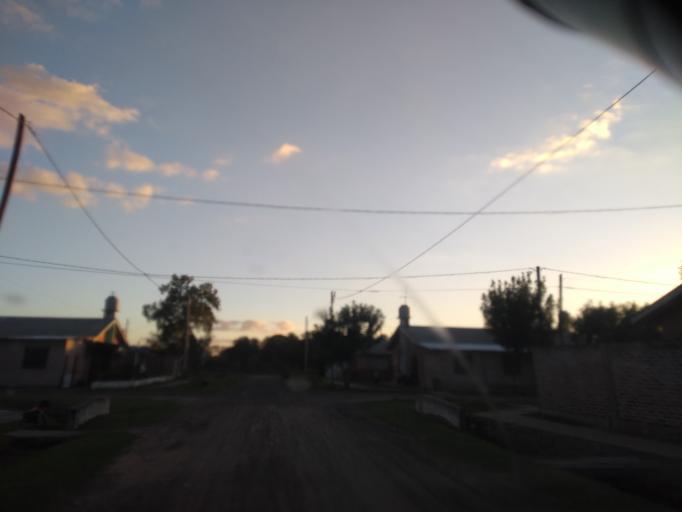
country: AR
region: Chaco
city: Fontana
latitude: -27.4202
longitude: -59.0523
